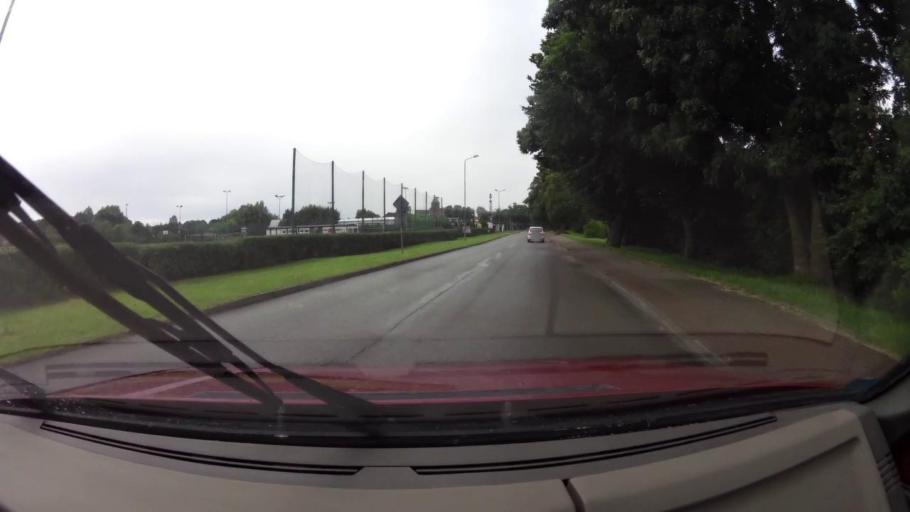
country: PL
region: West Pomeranian Voivodeship
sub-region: Powiat swidwinski
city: Swidwin
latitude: 53.7684
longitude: 15.7687
